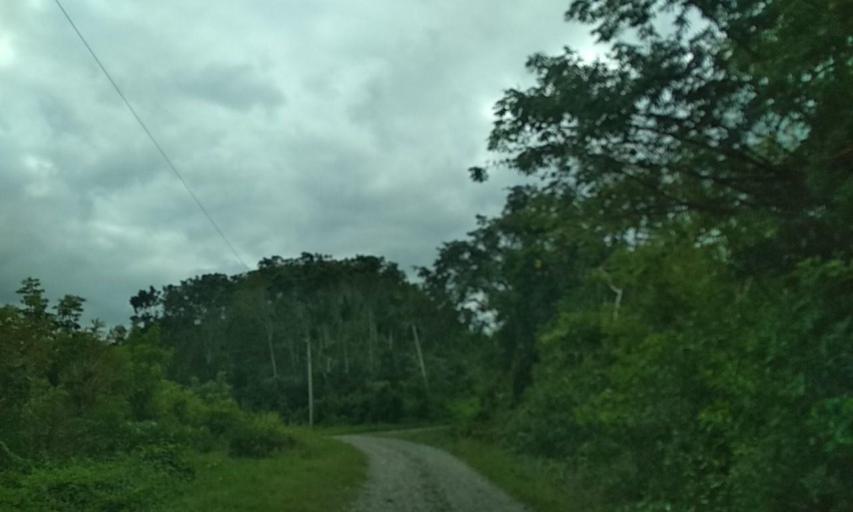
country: MX
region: Veracruz
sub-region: Papantla
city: Polutla
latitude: 20.5250
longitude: -97.2986
